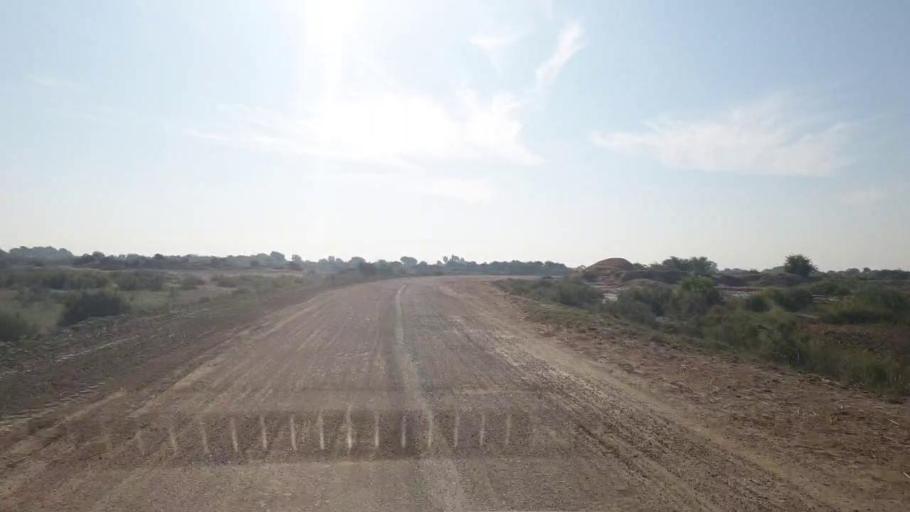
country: PK
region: Sindh
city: Rajo Khanani
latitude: 24.9695
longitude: 68.7942
